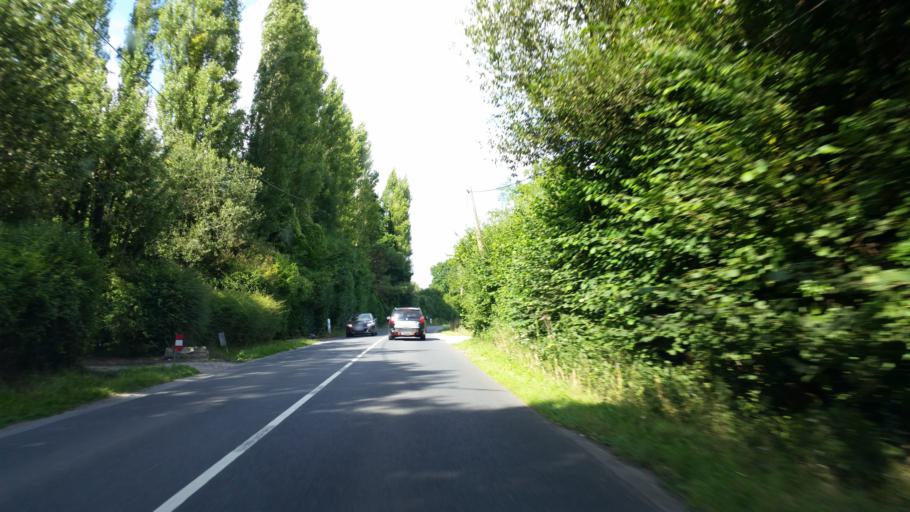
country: FR
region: Lower Normandy
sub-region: Departement du Calvados
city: Villers-sur-Mer
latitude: 49.2885
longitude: 0.0098
